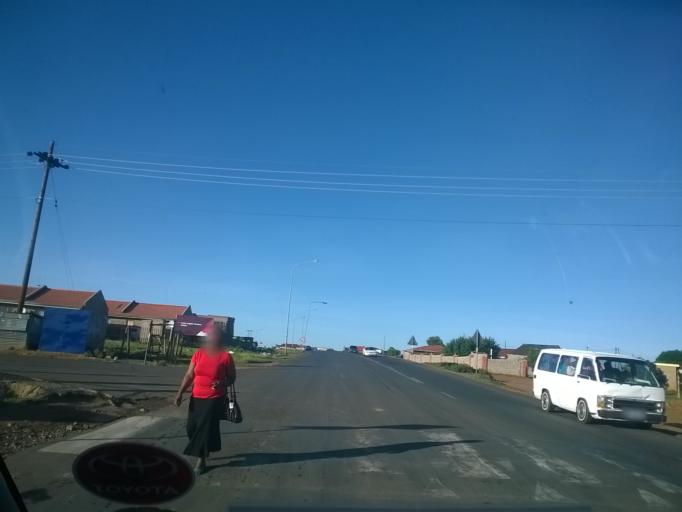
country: LS
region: Maseru
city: Maseru
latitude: -29.2725
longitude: 27.5322
